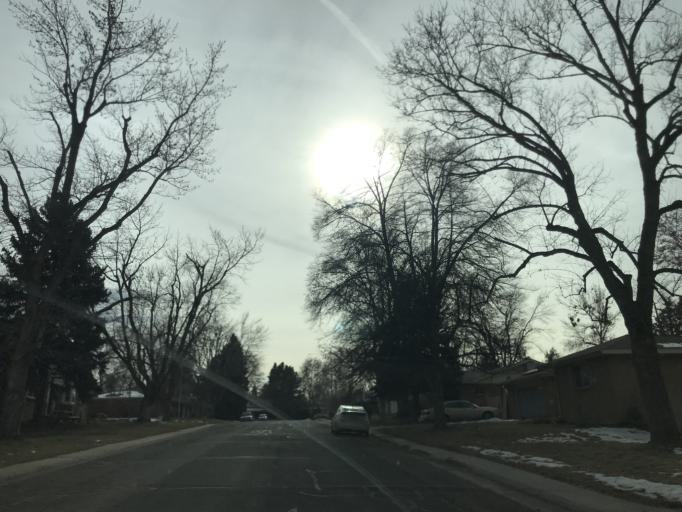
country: US
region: Colorado
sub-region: Arapahoe County
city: Columbine Valley
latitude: 39.5917
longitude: -105.0128
